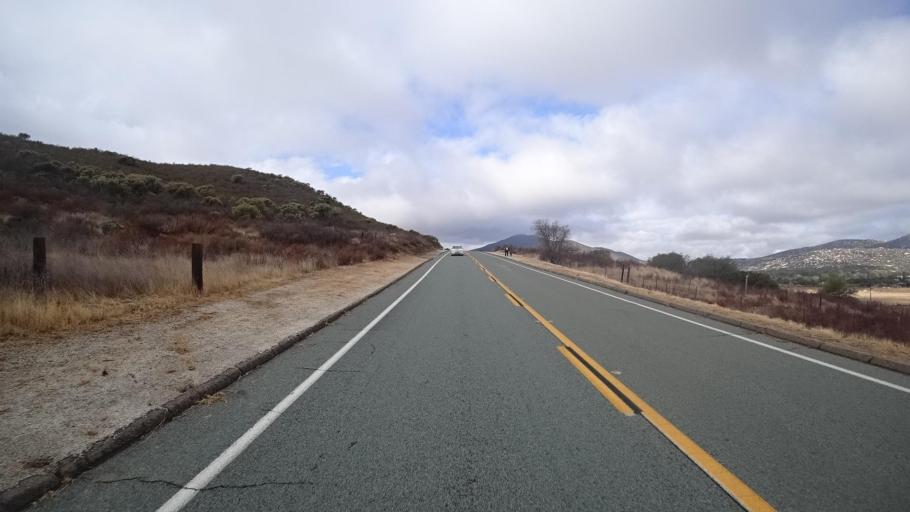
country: MX
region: Baja California
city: Tecate
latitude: 32.6151
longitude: -116.6037
